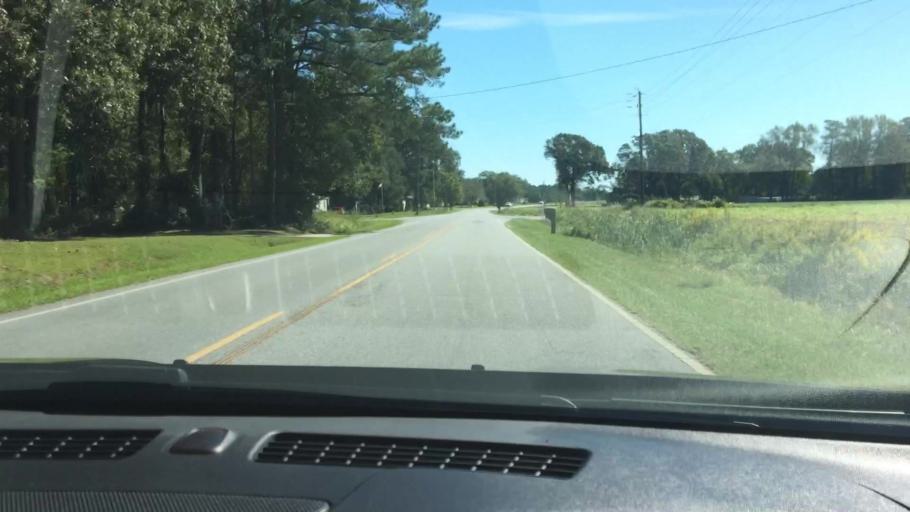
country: US
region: North Carolina
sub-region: Pitt County
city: Grifton
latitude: 35.3970
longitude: -77.3996
